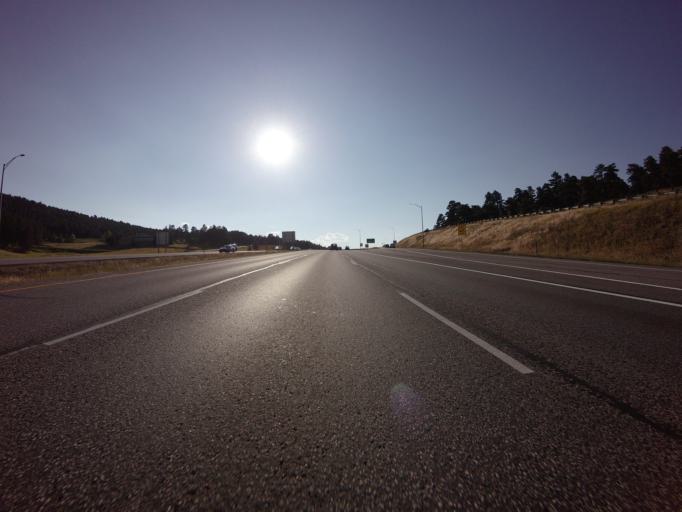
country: US
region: Colorado
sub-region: Jefferson County
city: Genesee
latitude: 39.7094
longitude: -105.2903
